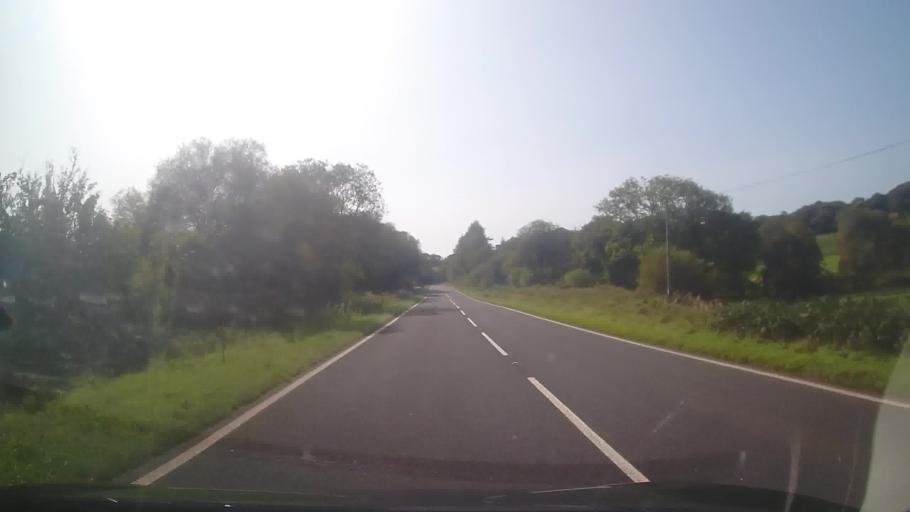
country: GB
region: Wales
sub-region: Sir Powys
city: Rhayader
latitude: 52.1266
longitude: -3.6157
